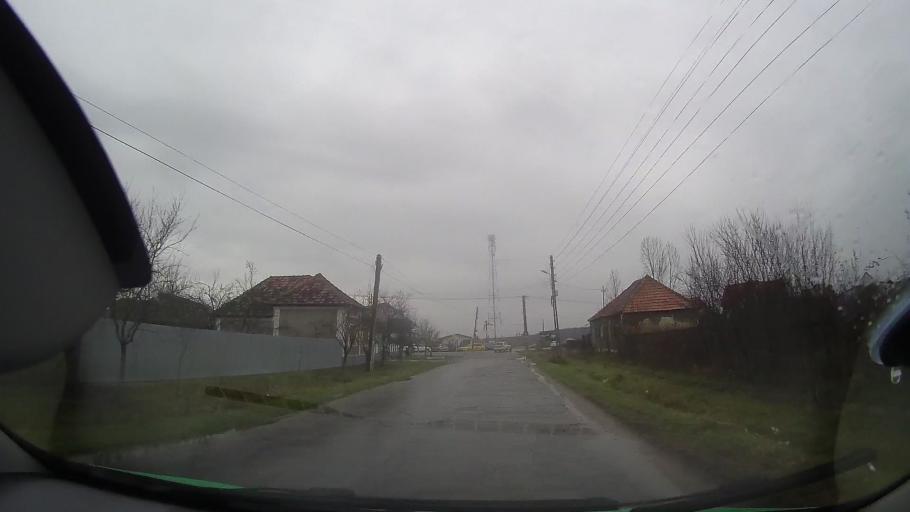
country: RO
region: Bihor
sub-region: Comuna Olcea
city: Olcea
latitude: 46.6840
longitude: 21.9673
